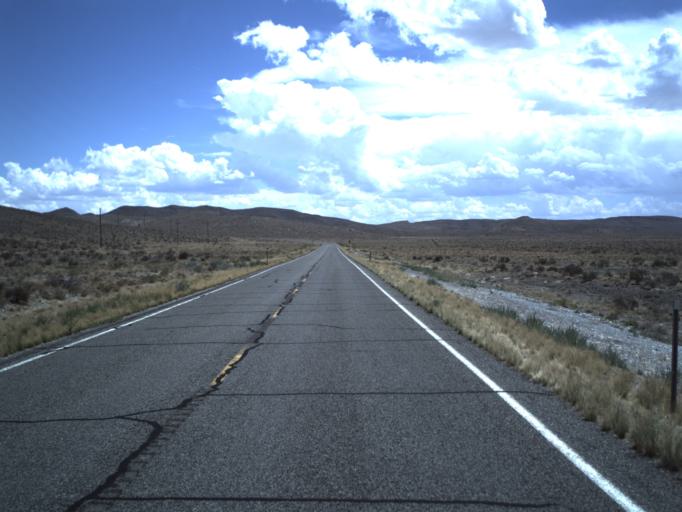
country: US
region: Utah
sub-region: Beaver County
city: Milford
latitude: 39.0265
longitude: -113.3744
